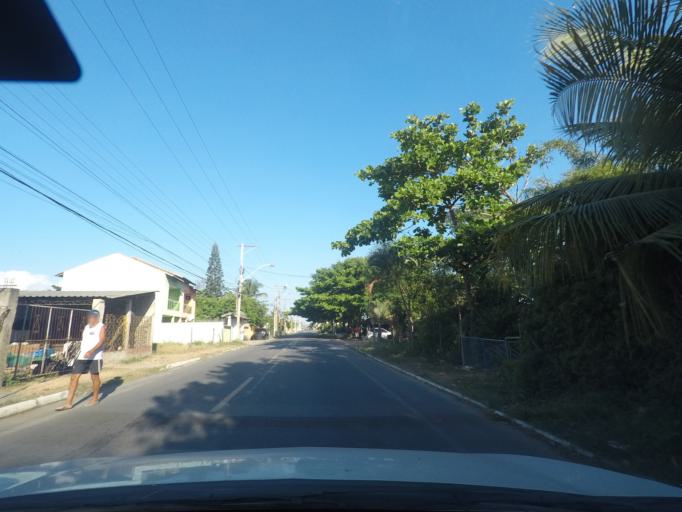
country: BR
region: Rio de Janeiro
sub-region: Marica
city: Marica
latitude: -22.9696
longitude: -42.9422
